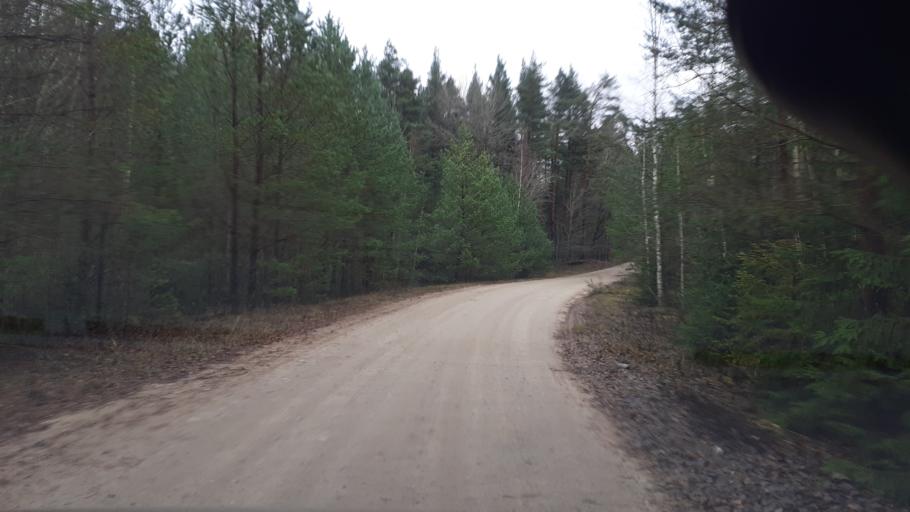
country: LV
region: Kuldigas Rajons
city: Kuldiga
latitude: 57.0322
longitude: 21.8732
